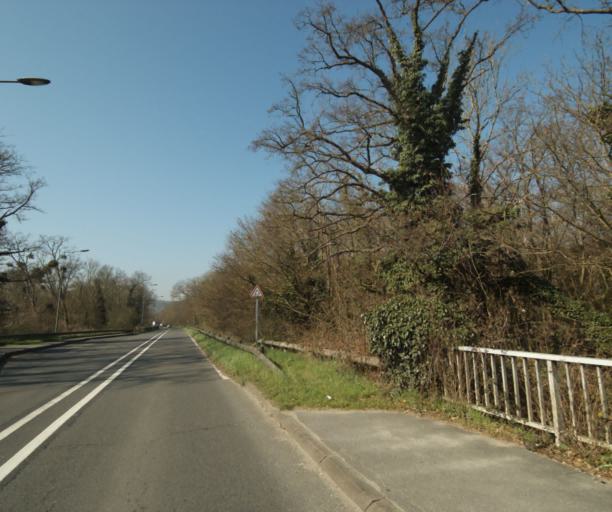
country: FR
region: Ile-de-France
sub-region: Departement du Val-d'Oise
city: Neuville-sur-Oise
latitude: 49.0226
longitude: 2.0557
